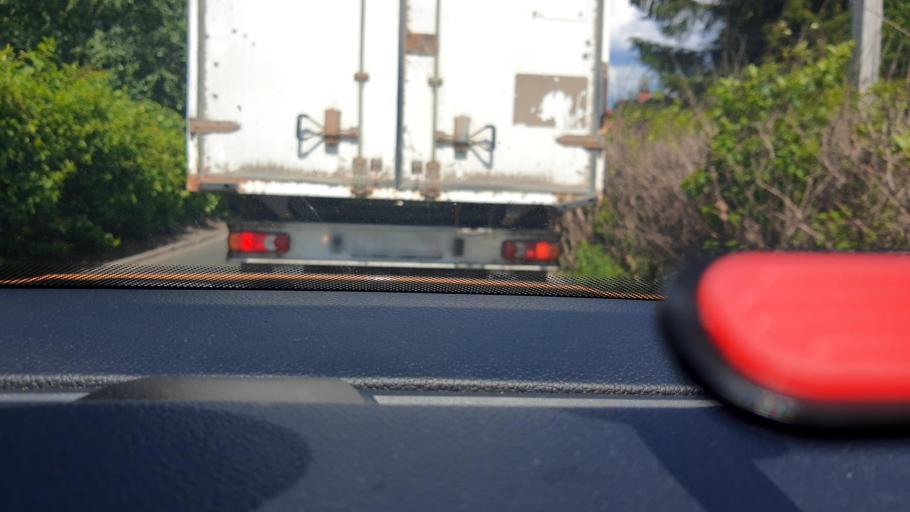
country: RU
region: Moskovskaya
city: Firsanovka
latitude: 55.9520
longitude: 37.2312
